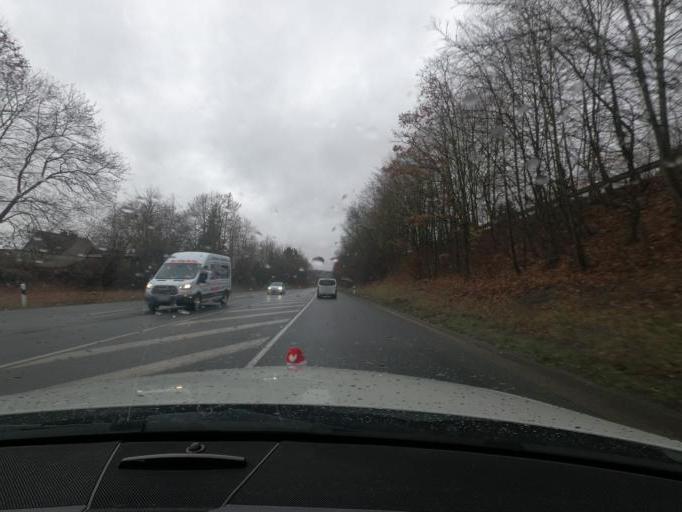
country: DE
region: Lower Saxony
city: Einbeck
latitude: 51.8000
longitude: 9.9235
